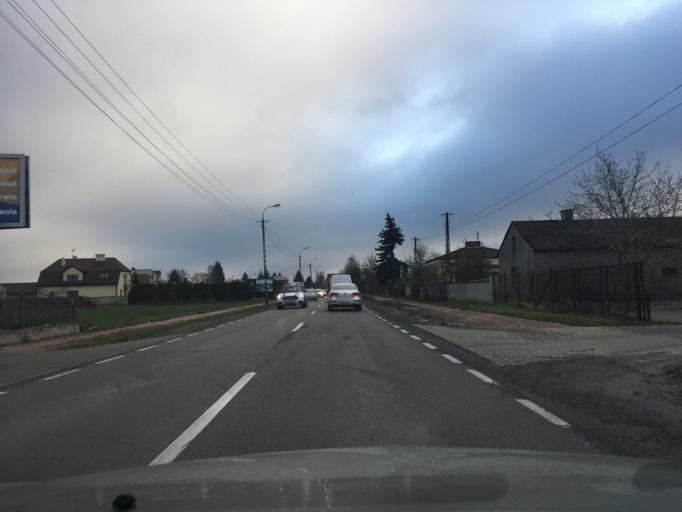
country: PL
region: Masovian Voivodeship
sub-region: Powiat piaseczynski
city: Lesznowola
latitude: 52.0846
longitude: 20.9542
